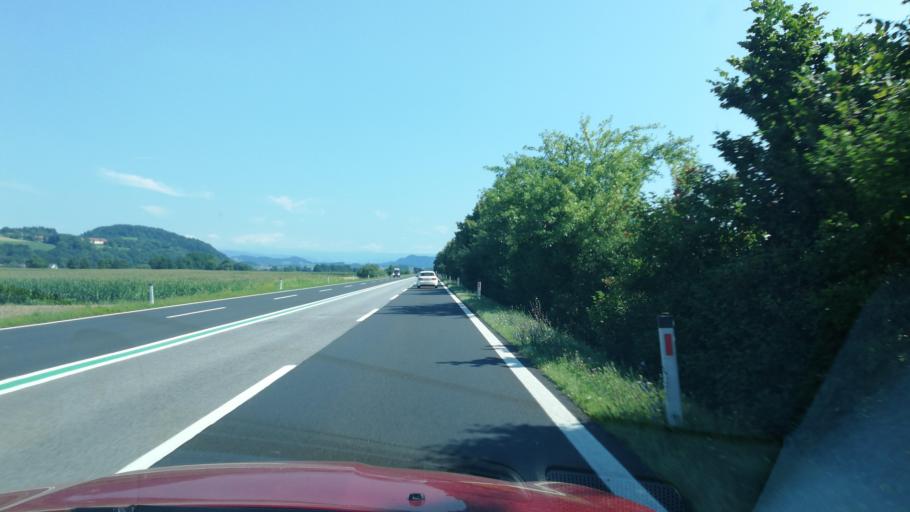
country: AT
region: Carinthia
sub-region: Politischer Bezirk Klagenfurt Land
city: Maria Saal
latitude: 46.6869
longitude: 14.3415
